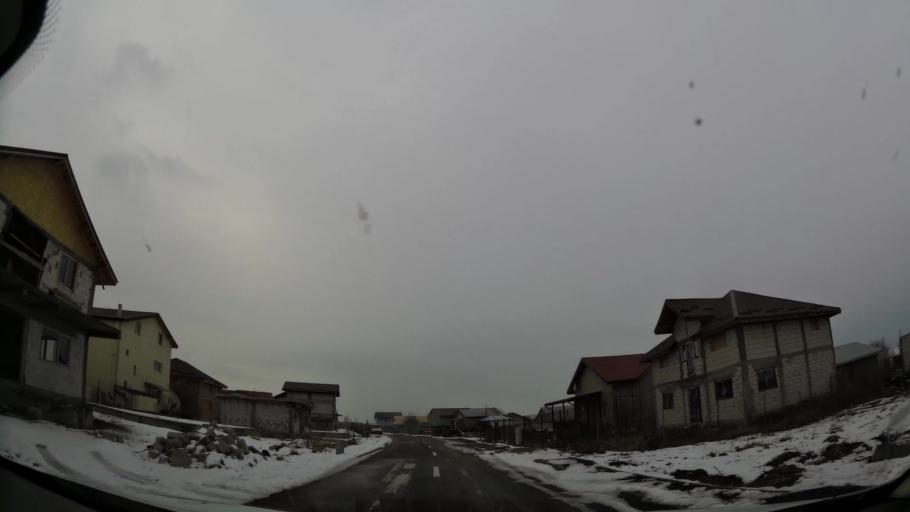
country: RO
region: Ilfov
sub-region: Comuna Tunari
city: Tunari
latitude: 44.5536
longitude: 26.1547
